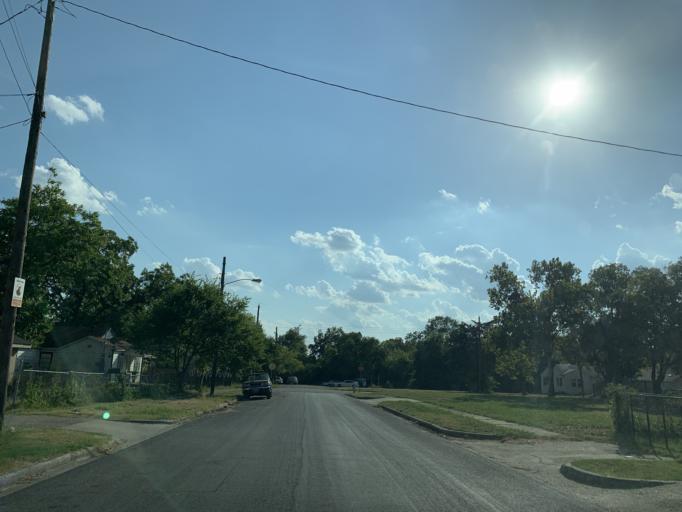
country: US
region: Texas
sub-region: Dallas County
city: Hutchins
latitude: 32.6962
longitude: -96.7813
